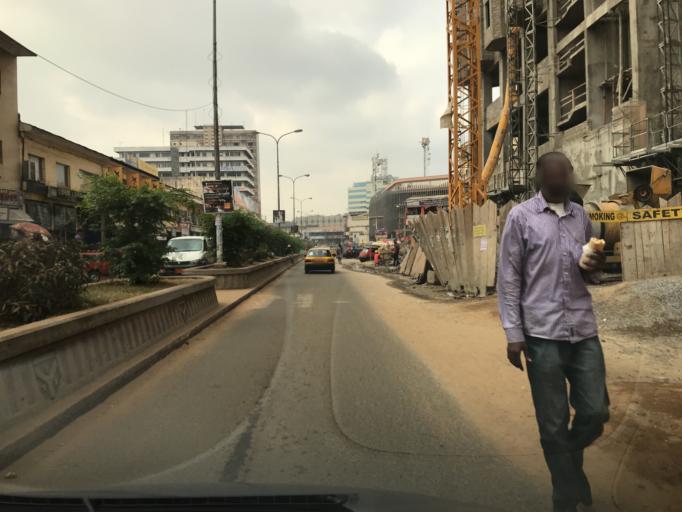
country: CM
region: Centre
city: Yaounde
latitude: 3.8656
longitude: 11.5204
